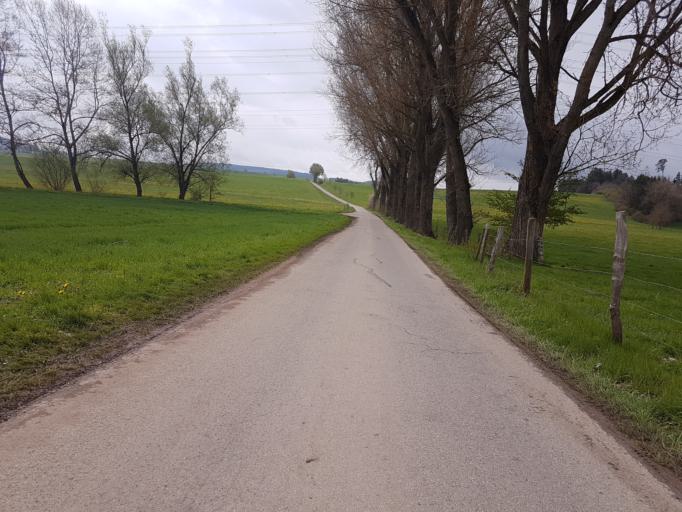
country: DE
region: Baden-Wuerttemberg
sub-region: Freiburg Region
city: Hufingen
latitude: 47.9143
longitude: 8.5177
